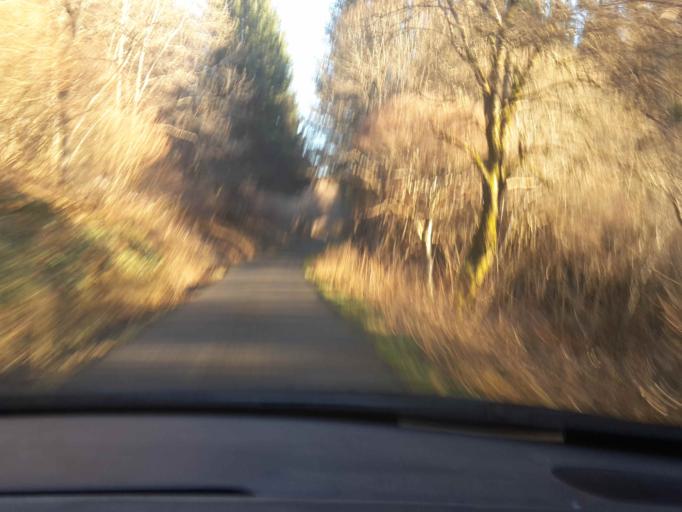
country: FR
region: Auvergne
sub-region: Departement du Cantal
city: Riom-es-Montagnes
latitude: 45.2225
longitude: 2.5725
